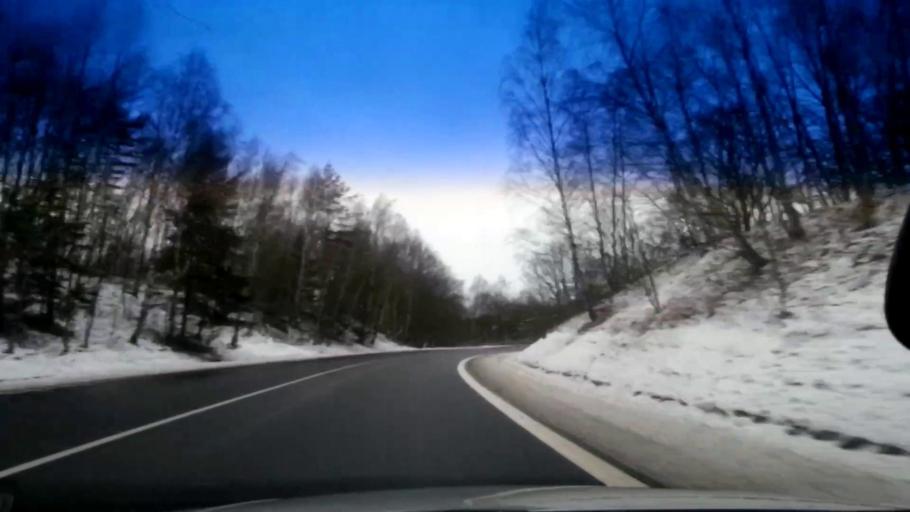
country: CZ
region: Karlovarsky
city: Hazlov
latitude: 50.1546
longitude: 12.2757
